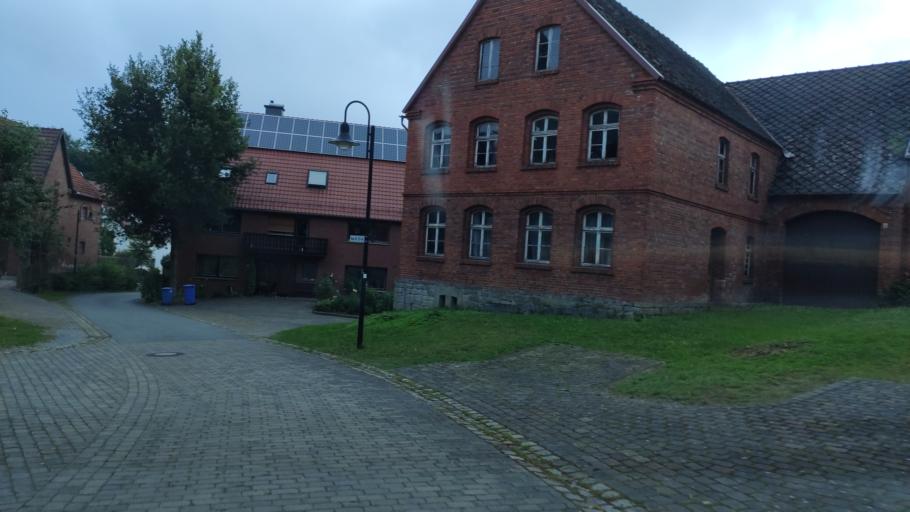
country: DE
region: North Rhine-Westphalia
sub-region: Regierungsbezirk Detmold
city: Schieder-Schwalenberg
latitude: 51.8407
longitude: 9.1754
